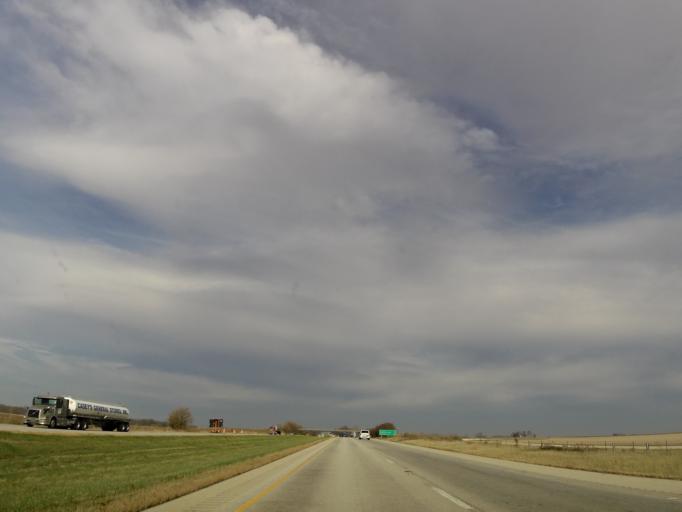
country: US
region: Illinois
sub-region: Knox County
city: Galesburg
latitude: 41.0013
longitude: -90.3352
